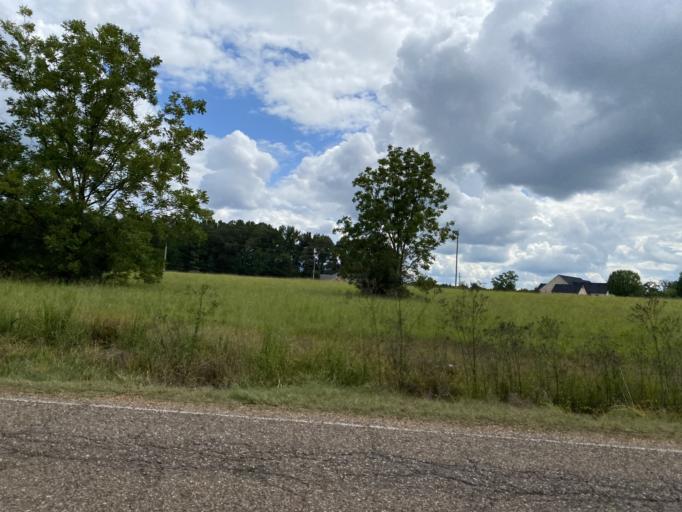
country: US
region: Mississippi
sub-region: Monroe County
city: Amory
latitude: 33.9744
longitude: -88.4429
